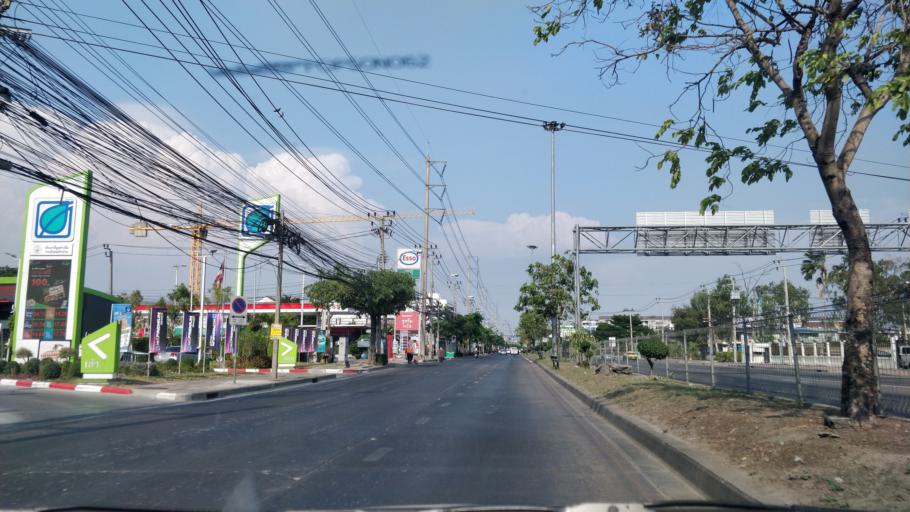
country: TH
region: Bangkok
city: Suan Luang
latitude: 13.7178
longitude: 100.6626
